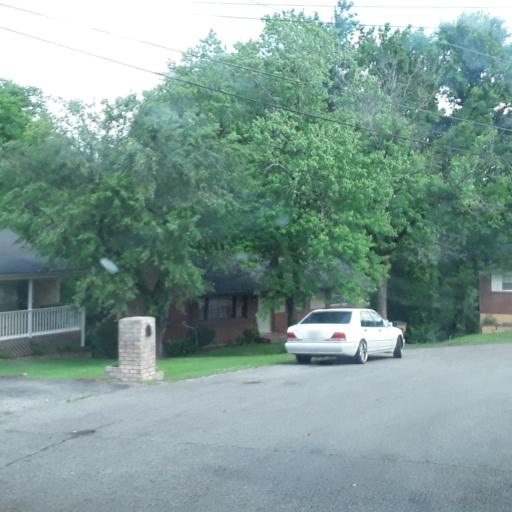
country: US
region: Tennessee
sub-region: Davidson County
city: Oak Hill
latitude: 36.1125
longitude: -86.7359
